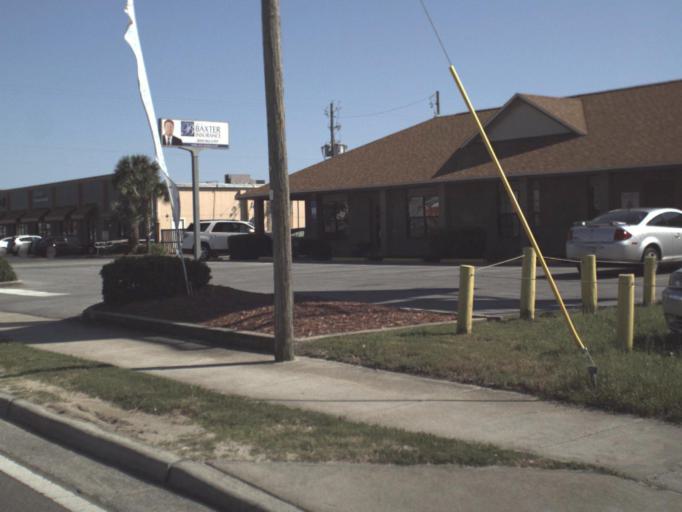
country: US
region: Florida
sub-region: Okaloosa County
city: Ocean City
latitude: 30.4437
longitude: -86.6029
